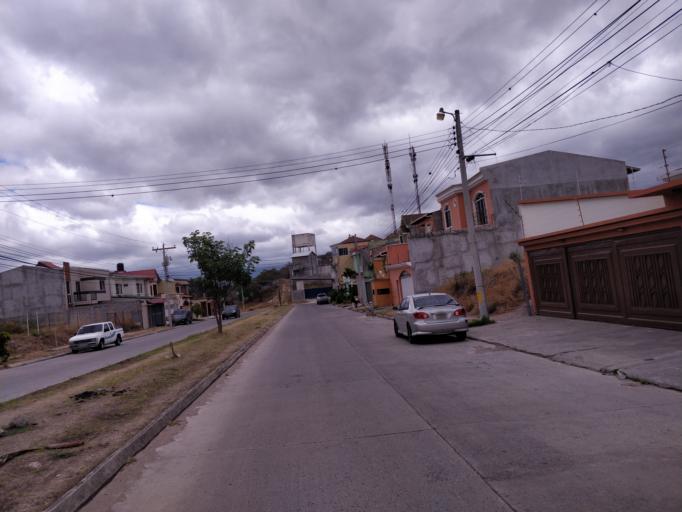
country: HN
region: Francisco Morazan
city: Yaguacire
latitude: 14.0343
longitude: -87.2390
